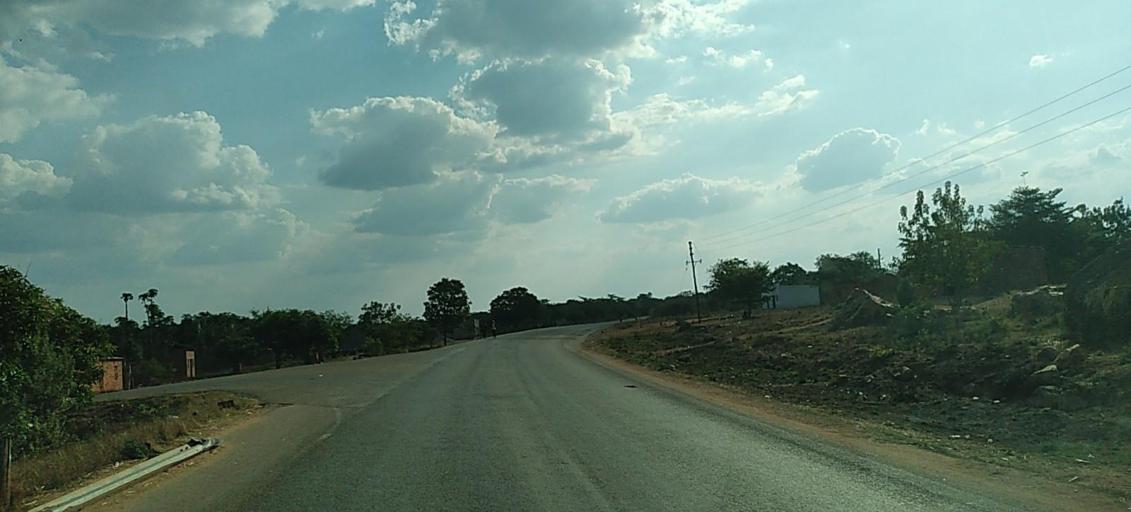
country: ZM
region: Copperbelt
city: Luanshya
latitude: -13.3617
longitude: 28.4128
